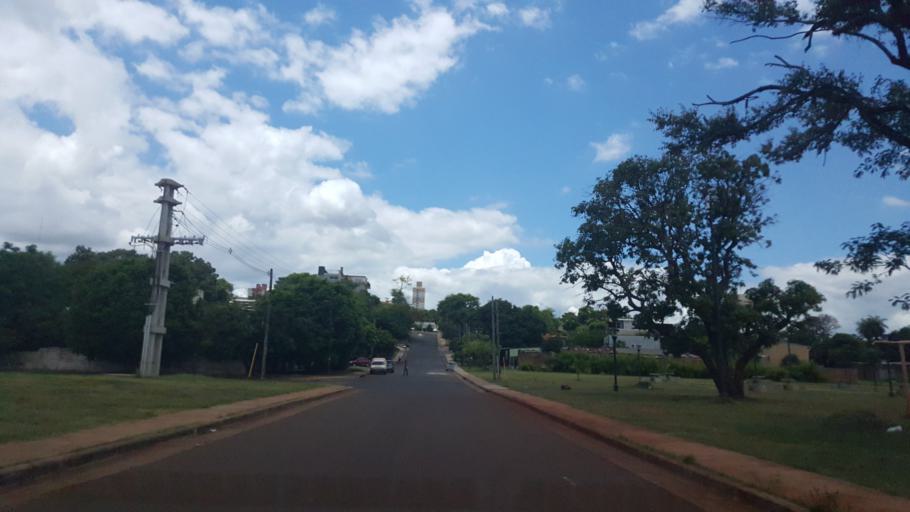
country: AR
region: Misiones
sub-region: Departamento de Capital
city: Posadas
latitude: -27.3569
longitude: -55.9029
